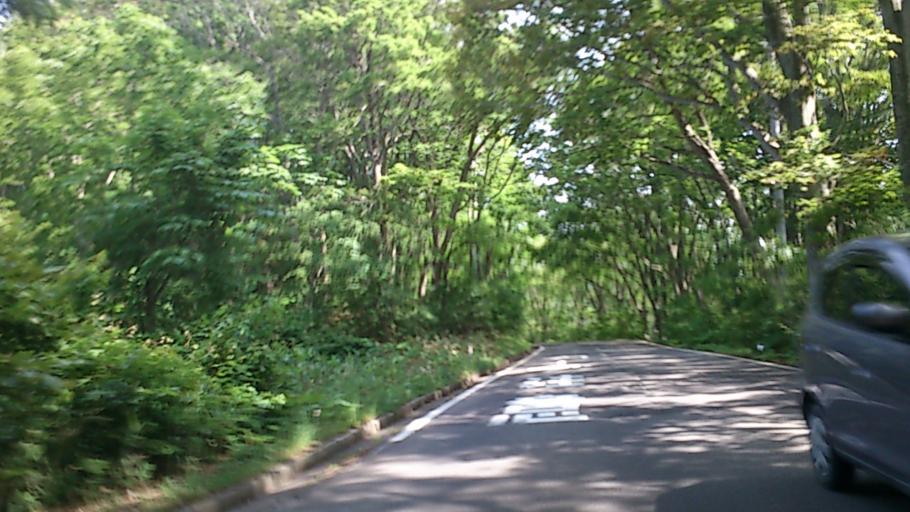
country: JP
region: Aomori
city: Aomori Shi
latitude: 40.7165
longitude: 140.8145
